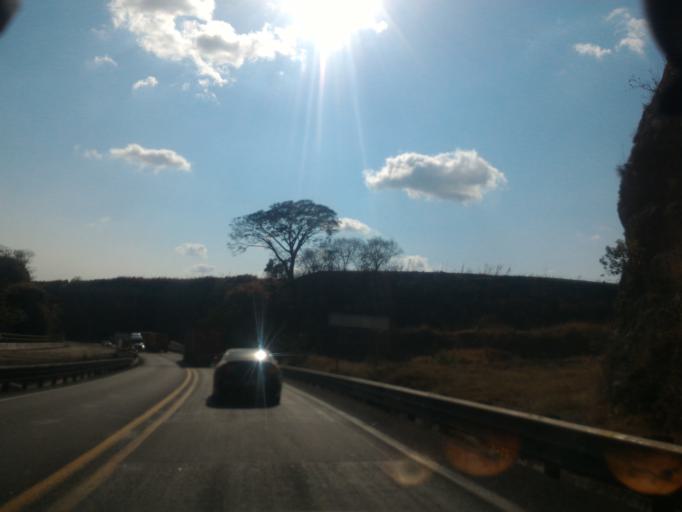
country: MX
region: Jalisco
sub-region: Tonila
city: San Marcos
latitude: 19.4512
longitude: -103.4724
